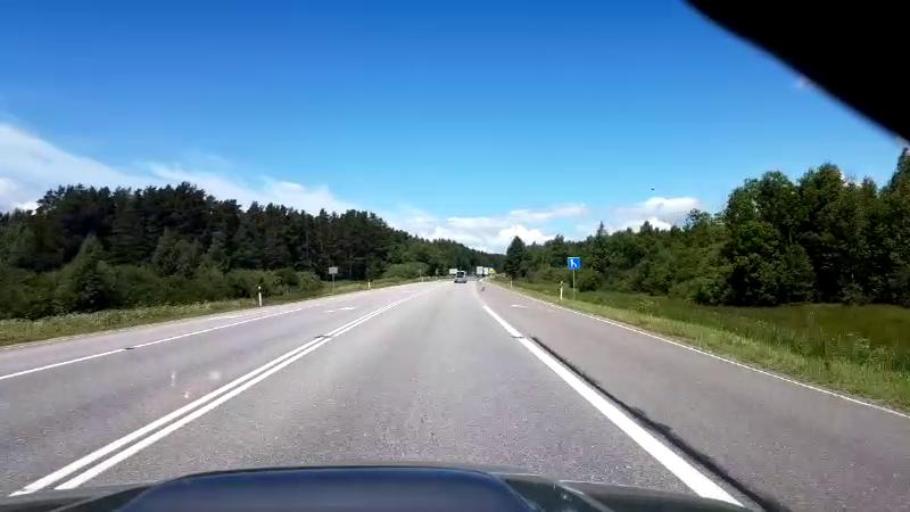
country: LV
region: Salacgrivas
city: Ainazi
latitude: 58.0888
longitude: 24.5081
